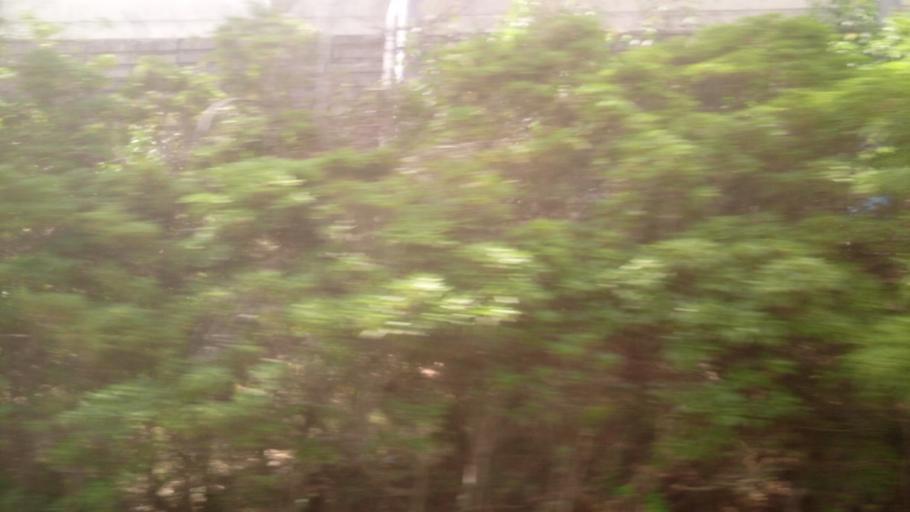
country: AU
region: New South Wales
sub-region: Blue Mountains Municipality
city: Lawson
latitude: -33.7229
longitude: 150.4160
